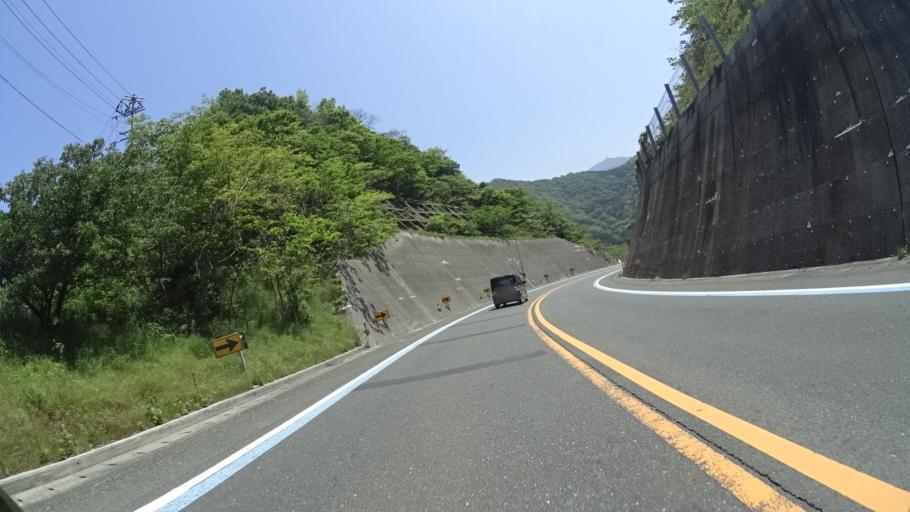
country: JP
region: Ehime
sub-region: Nishiuwa-gun
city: Ikata-cho
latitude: 33.5386
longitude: 132.4033
